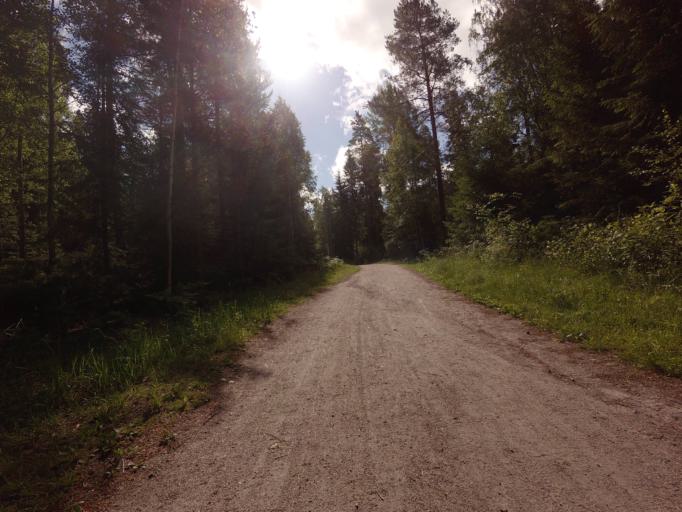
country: FI
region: Uusimaa
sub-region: Helsinki
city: Espoo
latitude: 60.1847
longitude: 24.6390
